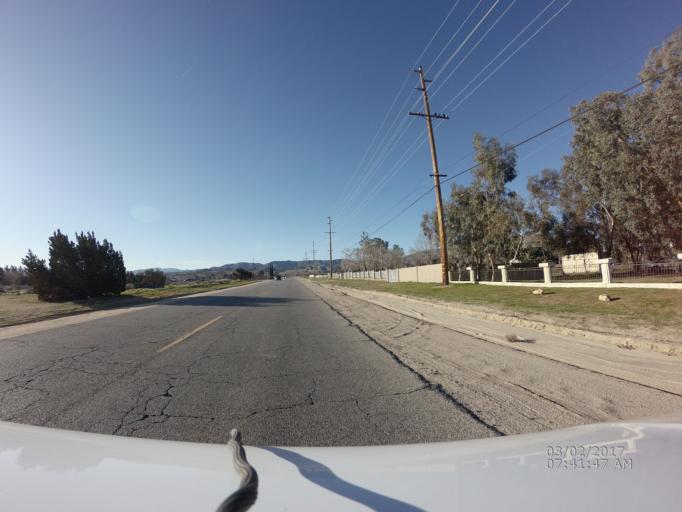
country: US
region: California
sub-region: Los Angeles County
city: Desert View Highlands
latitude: 34.6101
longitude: -118.1655
